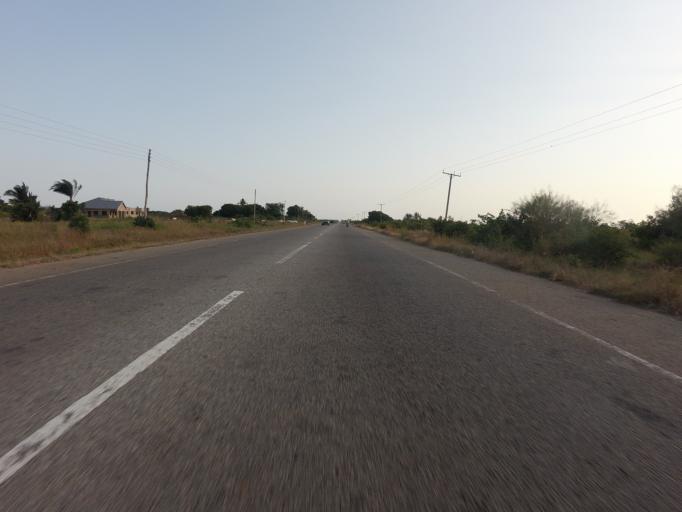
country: GH
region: Volta
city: Anloga
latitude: 6.0311
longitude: 0.6036
